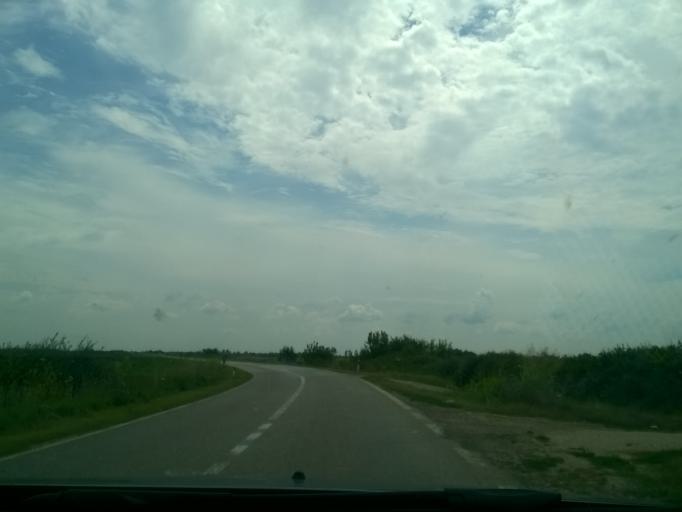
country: RS
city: Konak
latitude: 45.2968
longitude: 20.9268
